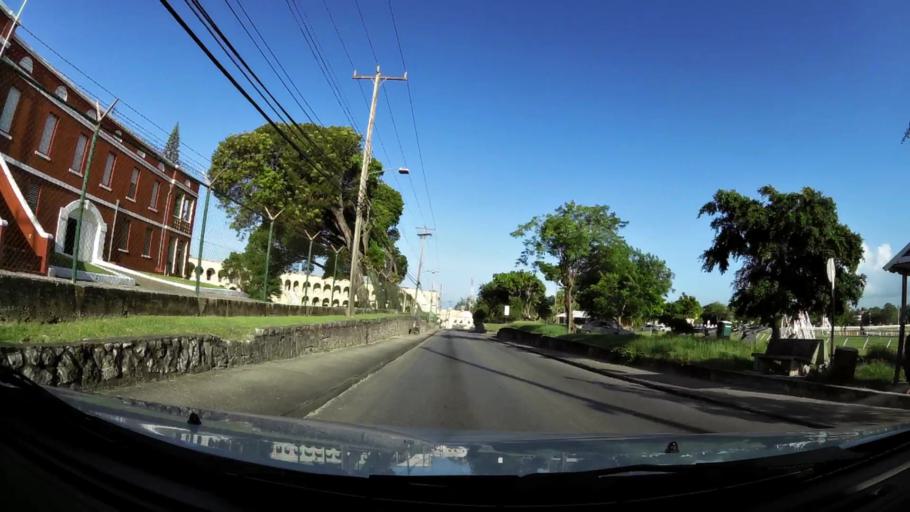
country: BB
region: Saint Michael
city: Bridgetown
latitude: 13.0792
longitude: -59.6063
